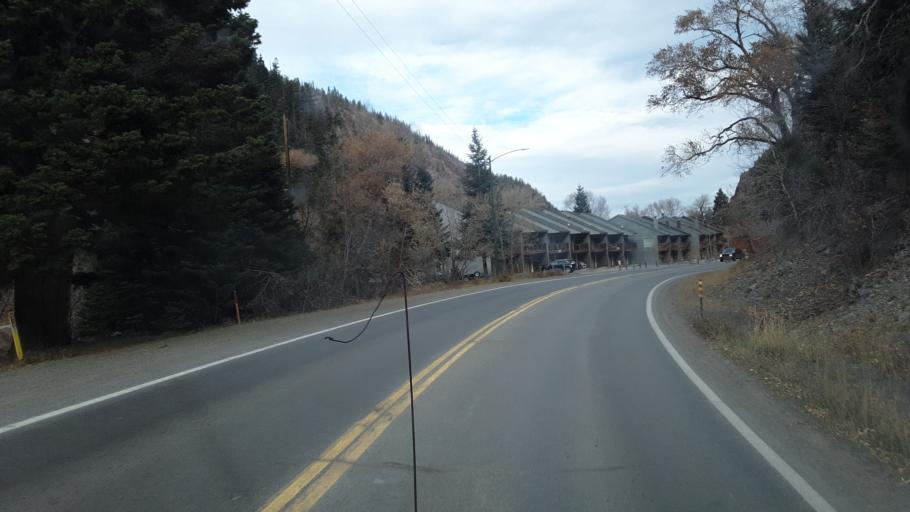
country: US
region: Colorado
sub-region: Ouray County
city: Ouray
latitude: 38.0304
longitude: -107.6743
